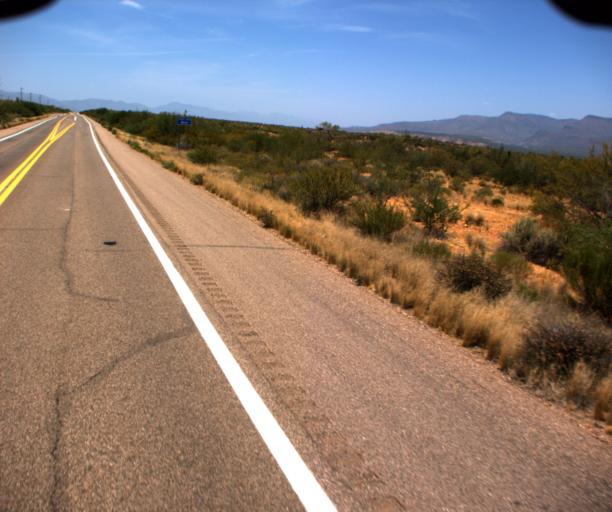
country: US
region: Arizona
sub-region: Gila County
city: Tonto Basin
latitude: 33.6415
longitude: -111.0842
